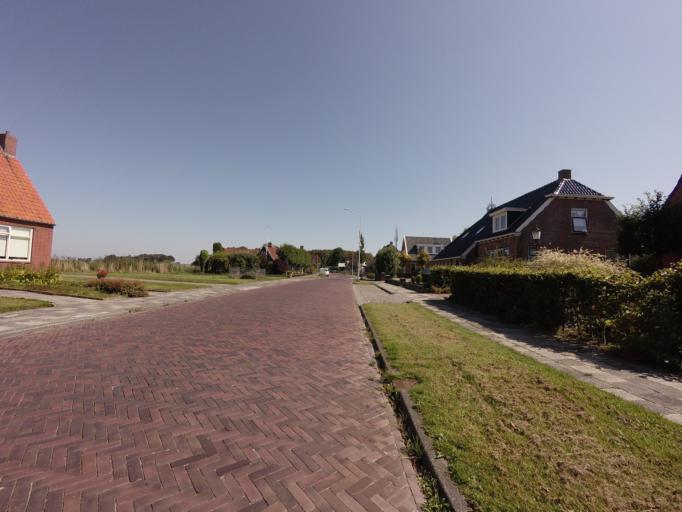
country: NL
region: Friesland
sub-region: Gemeente Dongeradeel
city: Anjum
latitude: 53.3807
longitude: 6.0512
